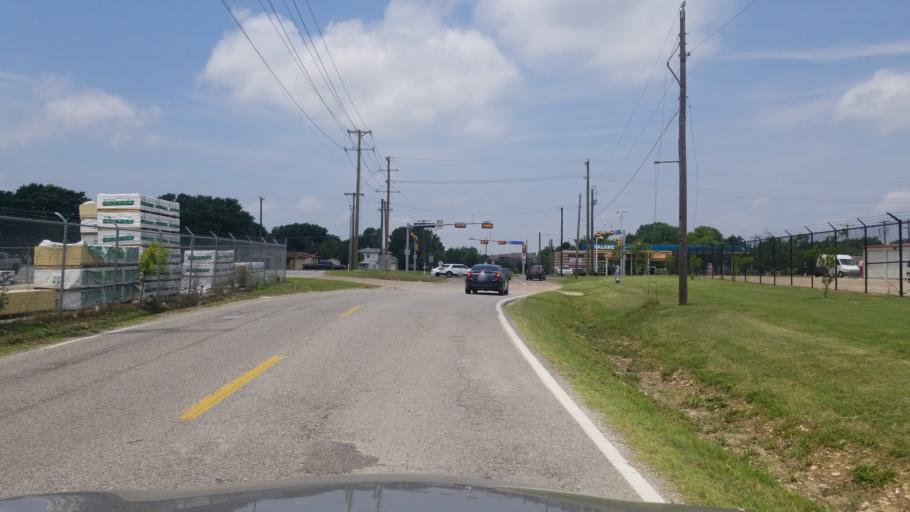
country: US
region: Texas
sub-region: Dallas County
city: Duncanville
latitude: 32.6746
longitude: -96.9075
